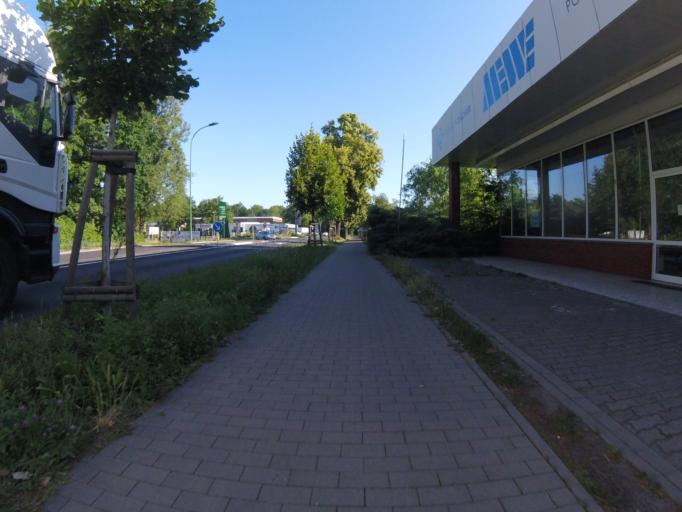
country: DE
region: Brandenburg
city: Konigs Wusterhausen
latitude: 52.2828
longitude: 13.6311
